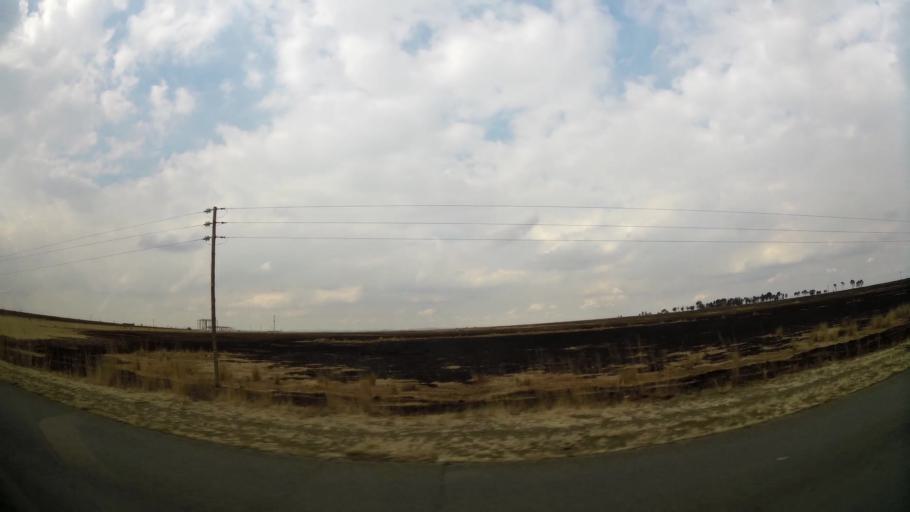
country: ZA
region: Orange Free State
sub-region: Fezile Dabi District Municipality
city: Sasolburg
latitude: -26.8709
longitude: 27.8874
